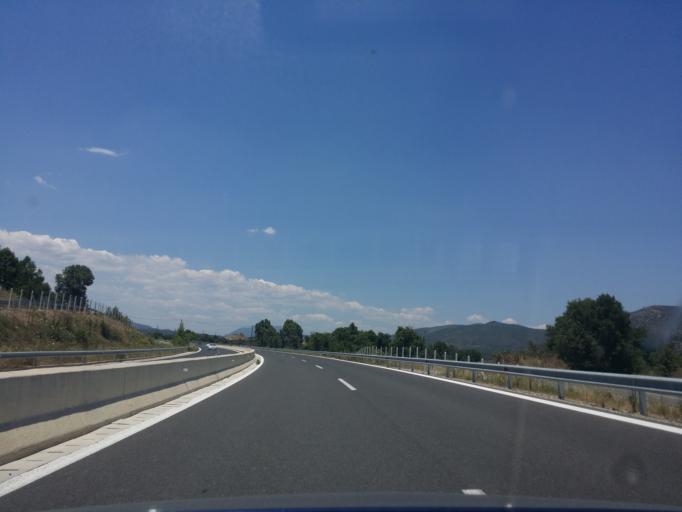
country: GR
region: Peloponnese
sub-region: Nomos Lakonias
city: Magoula
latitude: 37.1790
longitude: 22.3617
